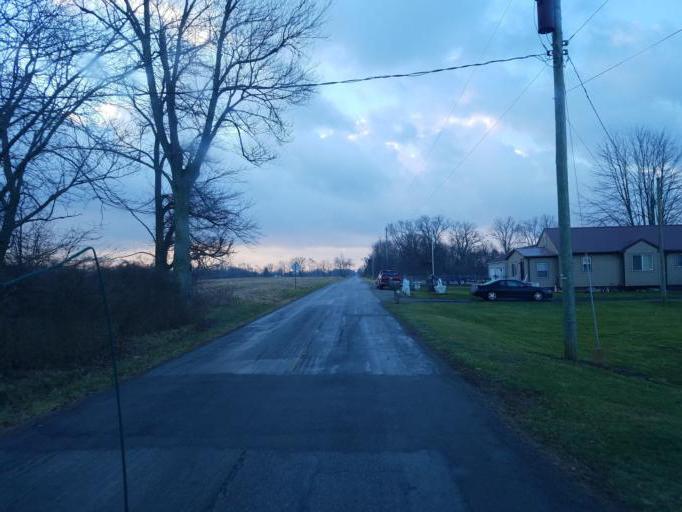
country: US
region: Ohio
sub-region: Marion County
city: Marion
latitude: 40.6116
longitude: -83.1888
